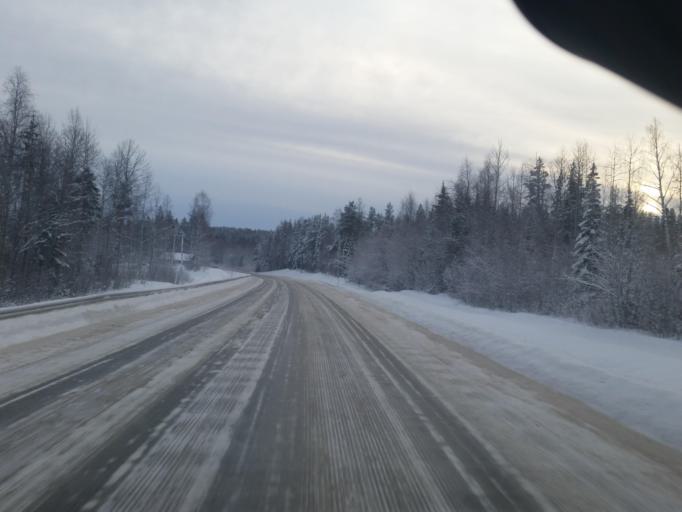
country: SE
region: Norrbotten
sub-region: Pitea Kommun
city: Norrfjarden
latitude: 65.6234
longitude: 21.4029
